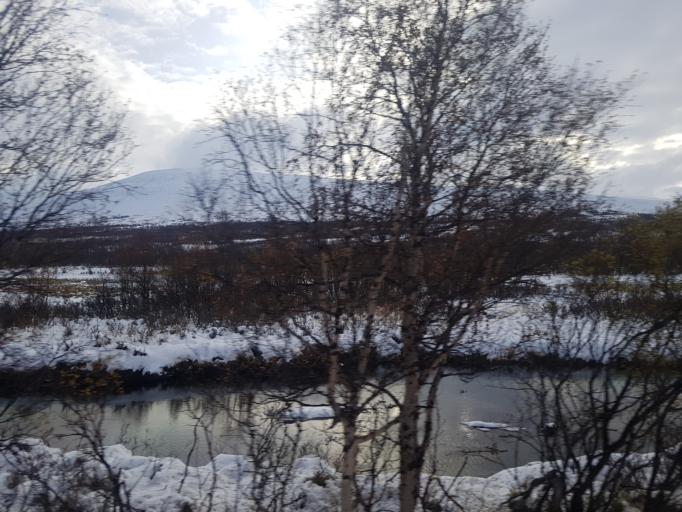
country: NO
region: Oppland
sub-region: Dovre
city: Dovre
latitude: 62.1257
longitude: 9.3064
